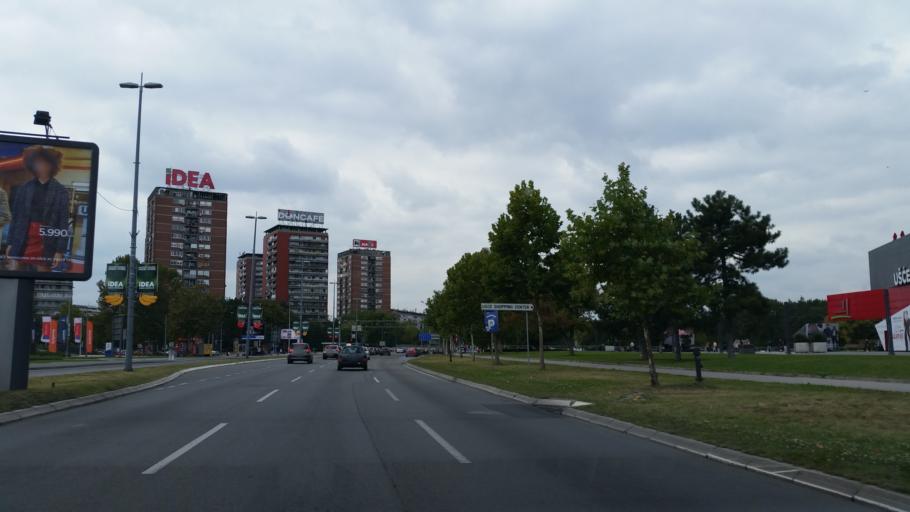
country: RS
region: Central Serbia
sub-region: Belgrade
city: Novi Beograd
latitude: 44.8144
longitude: 20.4370
